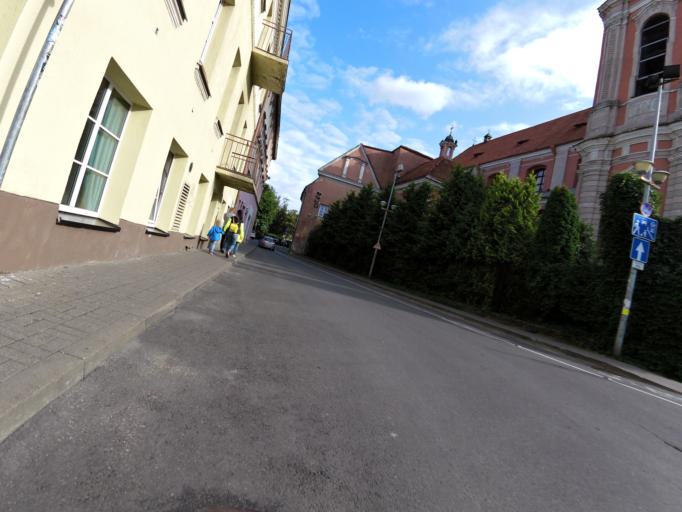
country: LT
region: Vilnius County
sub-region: Vilnius
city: Vilnius
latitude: 54.6761
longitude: 25.2842
